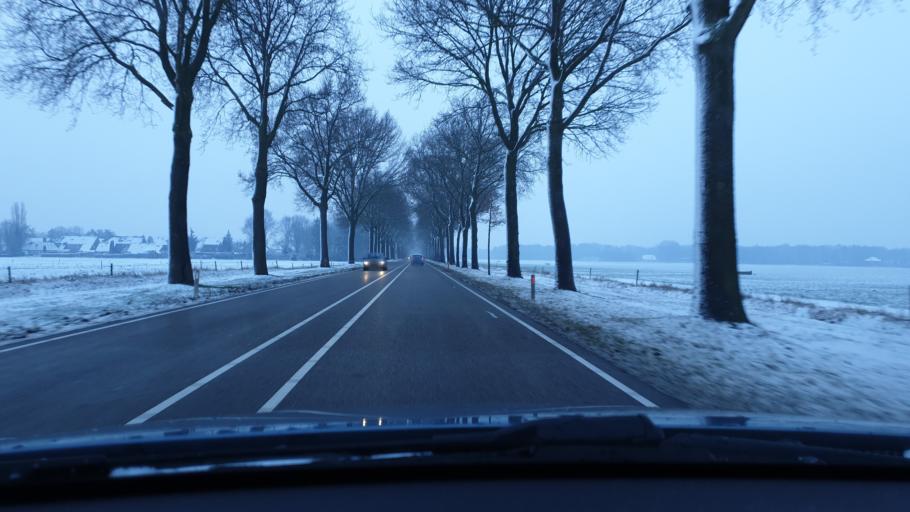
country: NL
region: North Brabant
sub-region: Gemeente Landerd
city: Zeeland
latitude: 51.7029
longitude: 5.6674
